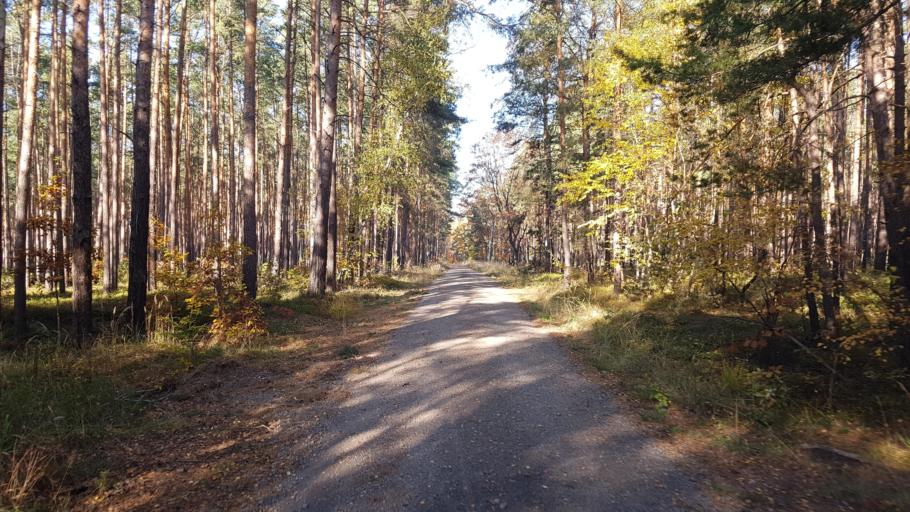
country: DE
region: Brandenburg
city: Ruckersdorf
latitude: 51.5589
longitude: 13.6249
